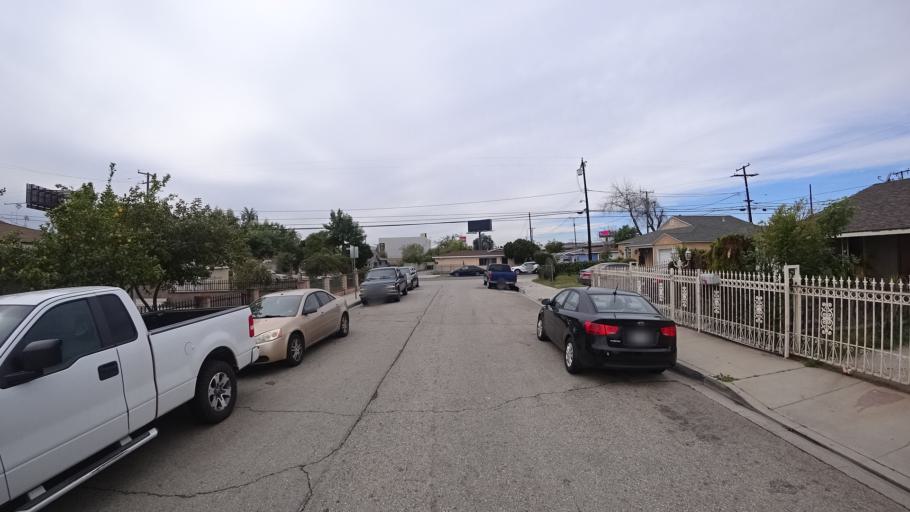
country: US
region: California
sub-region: Los Angeles County
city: West Puente Valley
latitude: 34.0685
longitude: -117.9858
